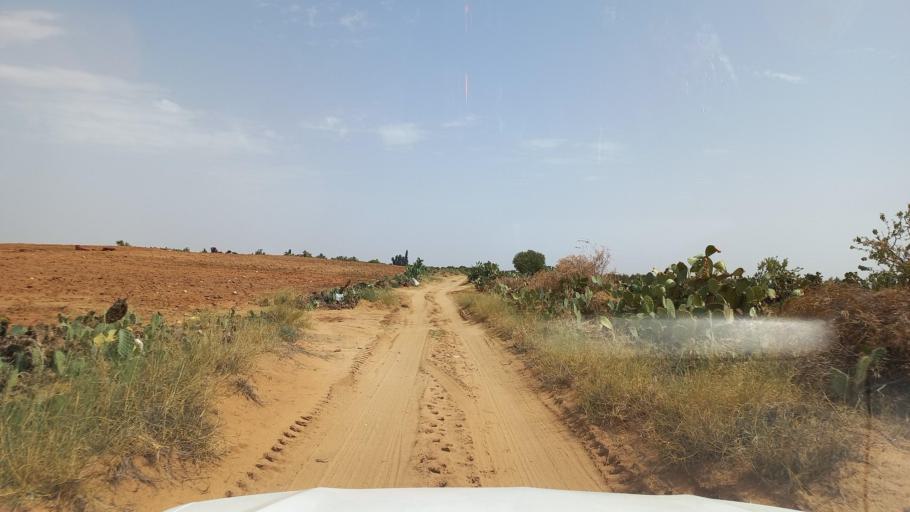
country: TN
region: Al Qasrayn
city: Kasserine
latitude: 35.2479
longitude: 9.0637
